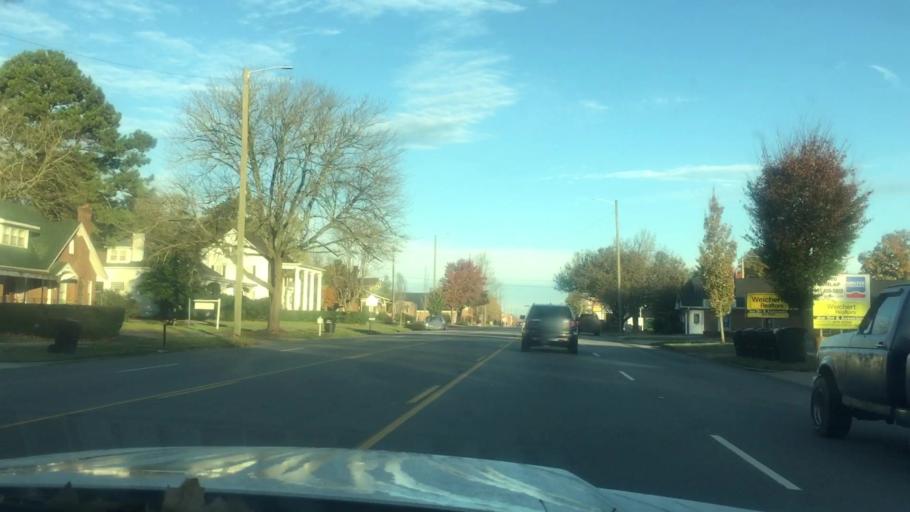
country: US
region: Tennessee
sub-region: Coffee County
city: Tullahoma
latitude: 35.3584
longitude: -86.2084
